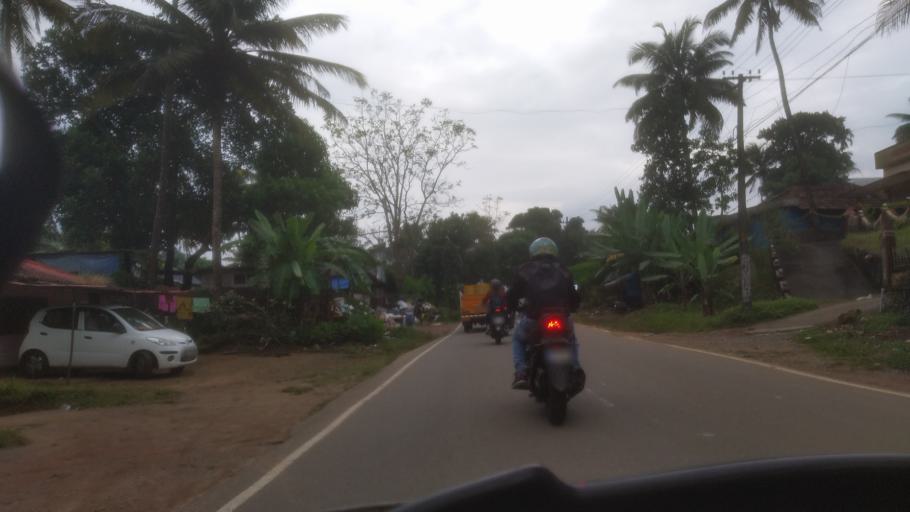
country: IN
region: Kerala
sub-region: Idukki
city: Munnar
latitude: 9.9934
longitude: 76.9786
